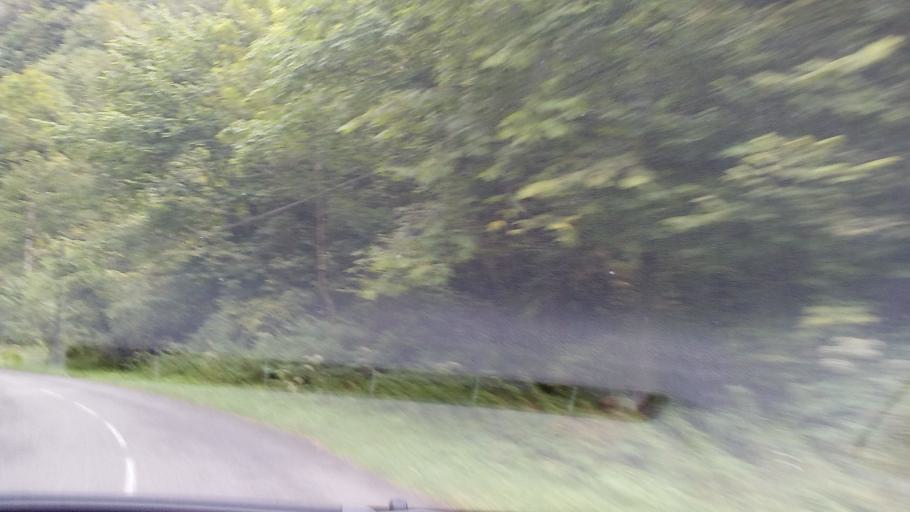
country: FR
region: Aquitaine
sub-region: Departement des Pyrenees-Atlantiques
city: Ogeu-les-Bains
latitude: 43.0790
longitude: -0.5792
